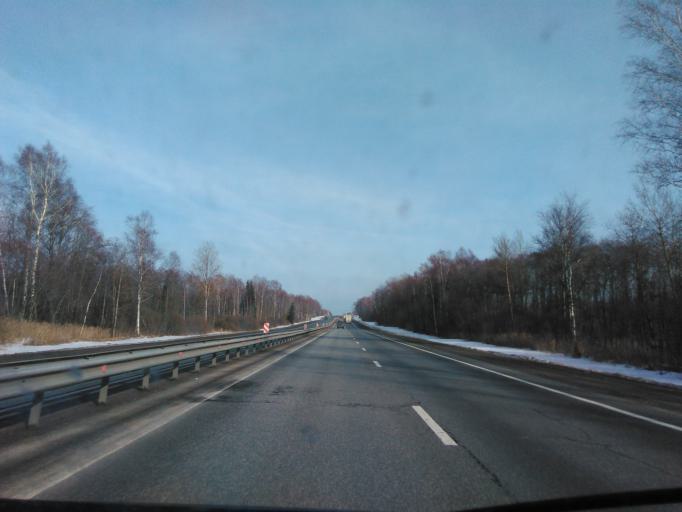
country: RU
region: Smolensk
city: Kholm-Zhirkovskiy
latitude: 55.1874
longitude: 33.7389
